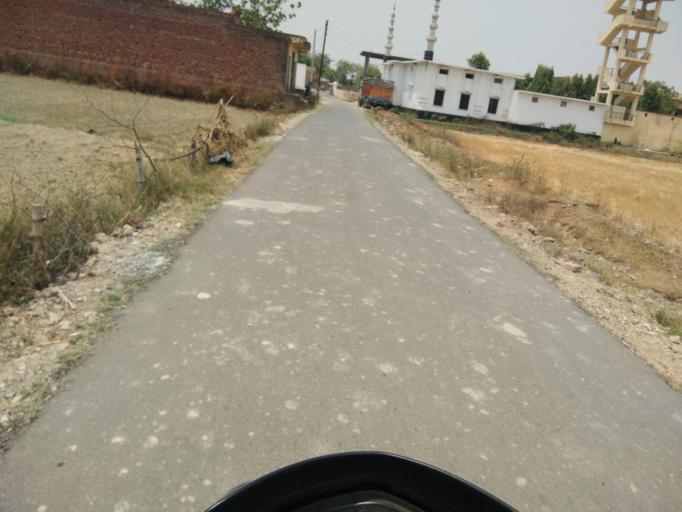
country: IN
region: Uttar Pradesh
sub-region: Ghazipur
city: Zamania
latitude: 25.4393
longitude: 83.6843
